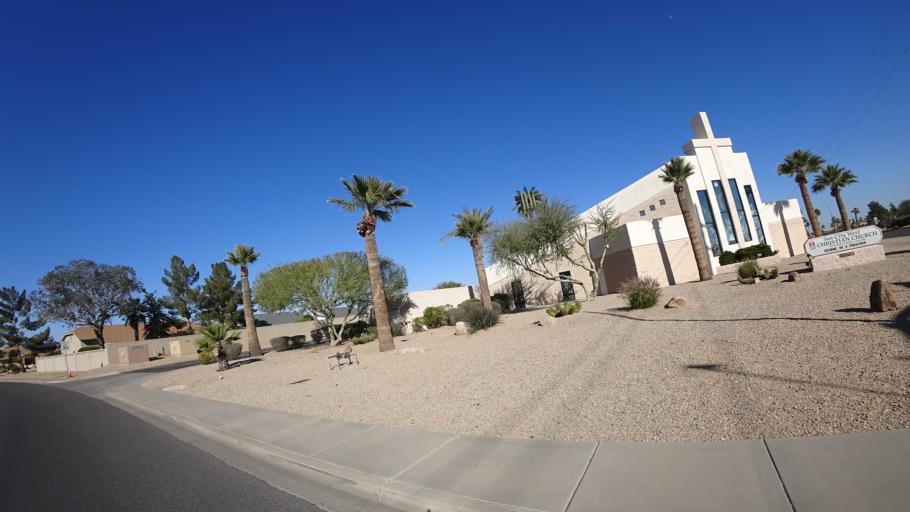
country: US
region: Arizona
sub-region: Maricopa County
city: Sun City West
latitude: 33.6728
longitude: -112.3795
